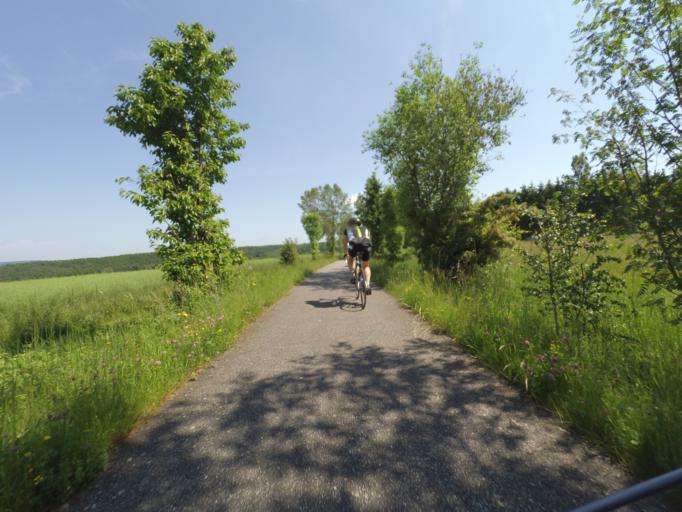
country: DE
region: Rheinland-Pfalz
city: Lingerhahn
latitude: 50.0948
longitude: 7.5700
